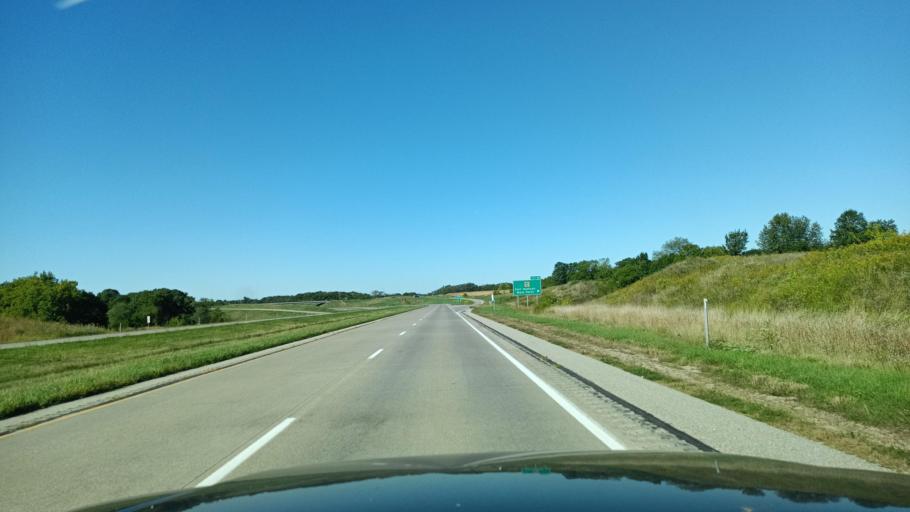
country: US
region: Iowa
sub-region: Lee County
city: Fort Madison
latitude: 40.6706
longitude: -91.3488
